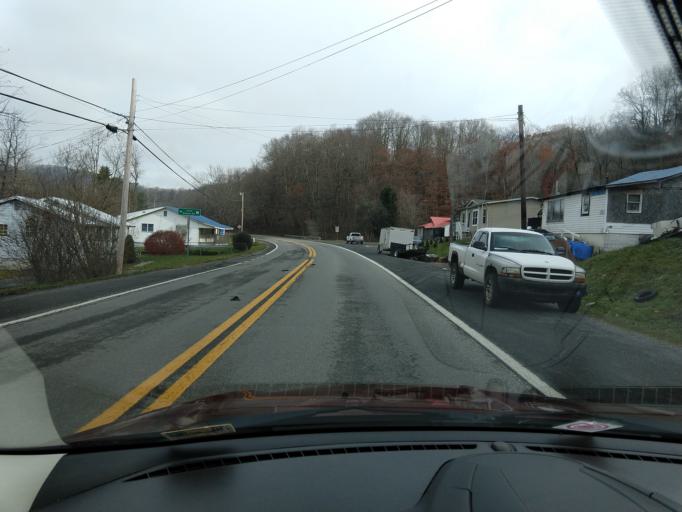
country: US
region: West Virginia
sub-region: Greenbrier County
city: Rainelle
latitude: 38.0437
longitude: -80.7238
